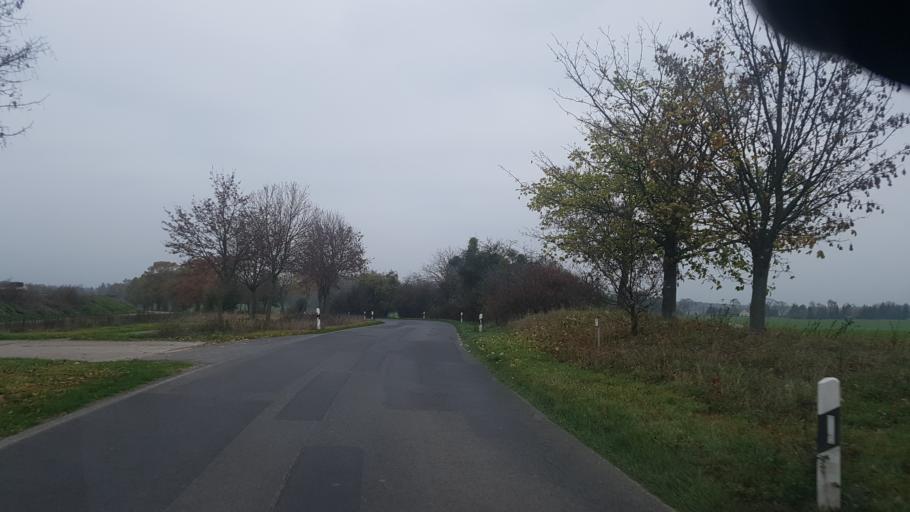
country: DE
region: Brandenburg
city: Schonermark
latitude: 52.9106
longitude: 13.1377
